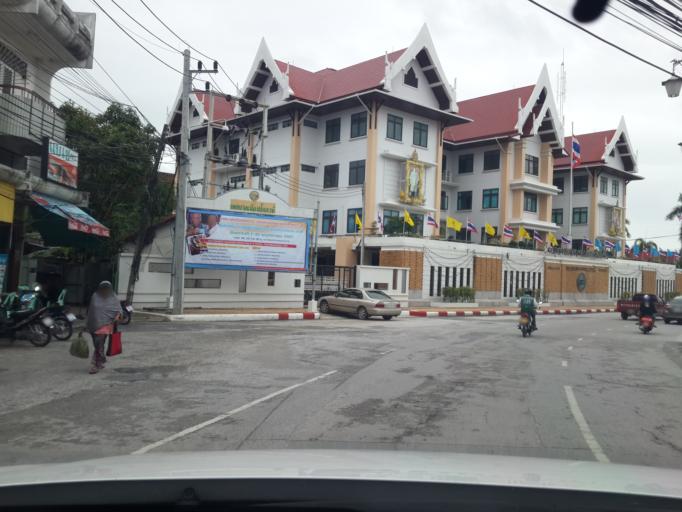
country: TH
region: Pattani
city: Pattani
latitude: 6.8661
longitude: 101.2515
